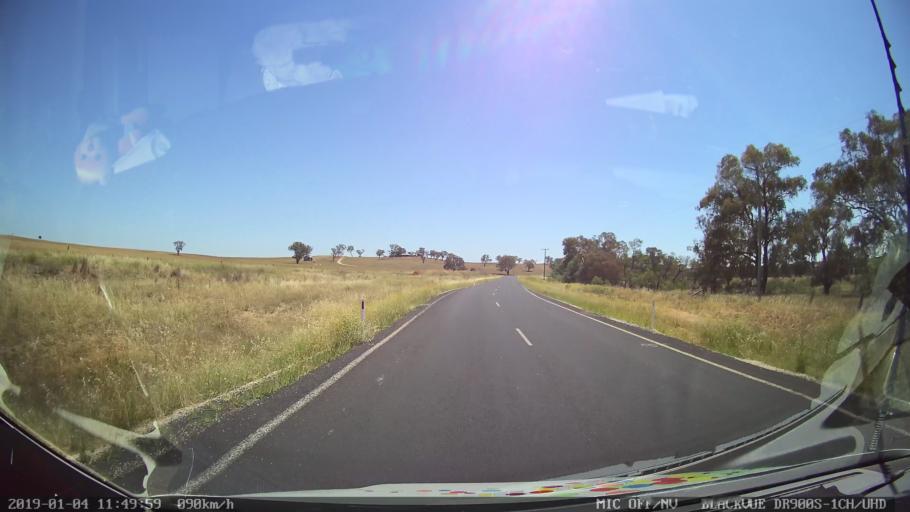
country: AU
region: New South Wales
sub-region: Cabonne
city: Molong
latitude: -32.9121
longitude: 148.7552
